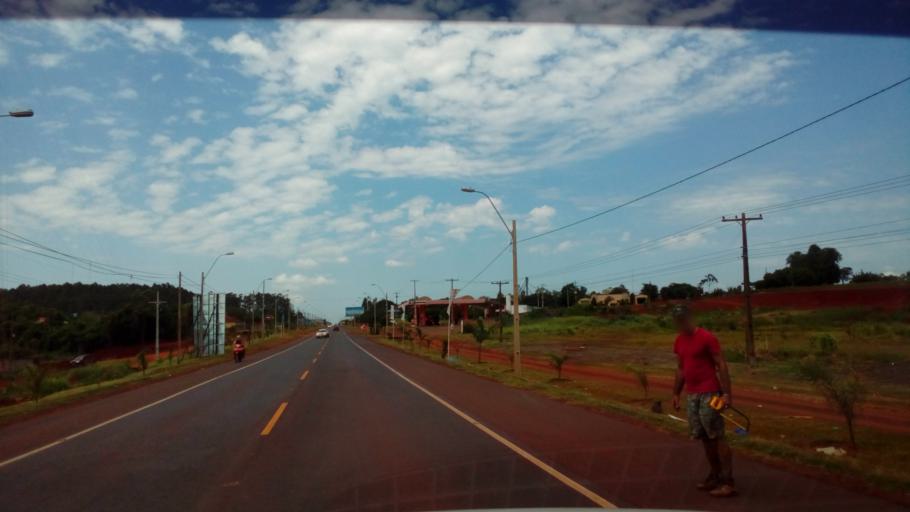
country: PY
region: Alto Parana
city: Santa Rita
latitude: -25.7627
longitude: -55.0648
